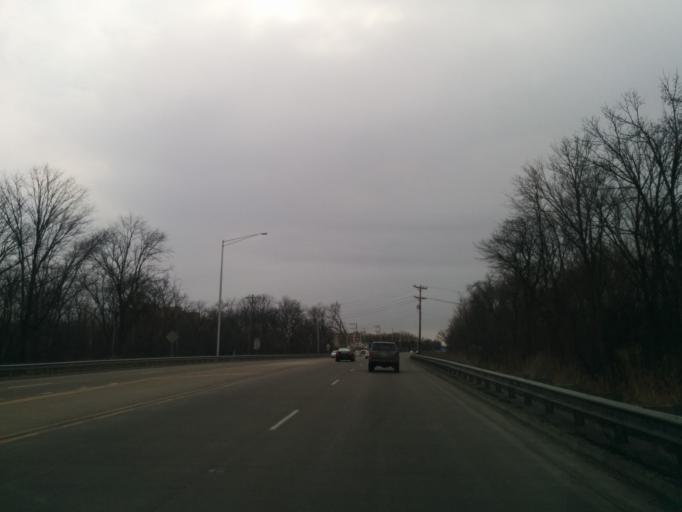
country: US
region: Illinois
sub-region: Cook County
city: Prospect Heights
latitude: 42.1034
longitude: -87.8862
